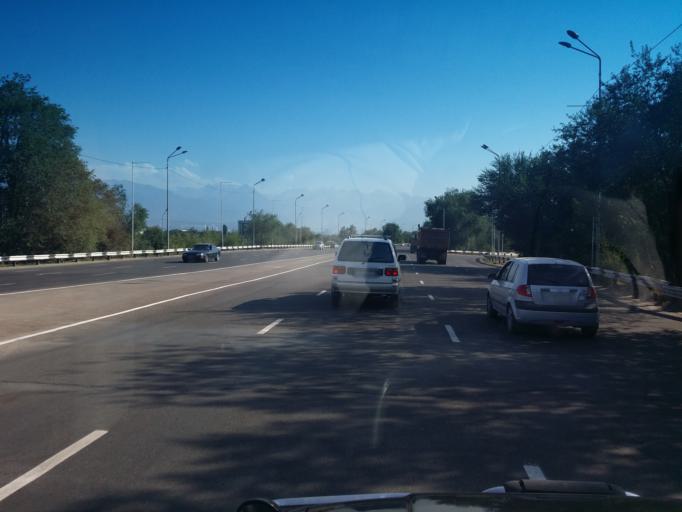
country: KZ
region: Almaty Oblysy
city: Pervomayskiy
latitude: 43.3533
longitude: 76.9382
